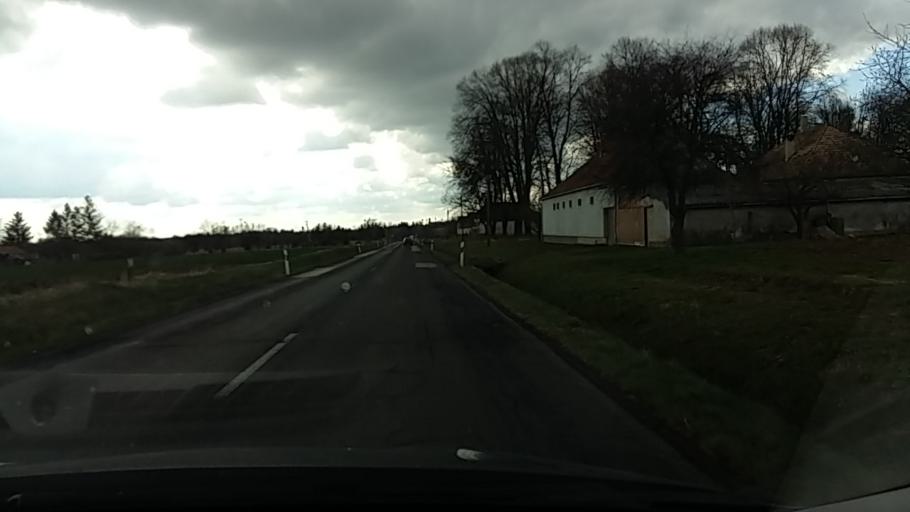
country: HU
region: Somogy
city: Bohonye
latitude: 46.4210
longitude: 17.3816
